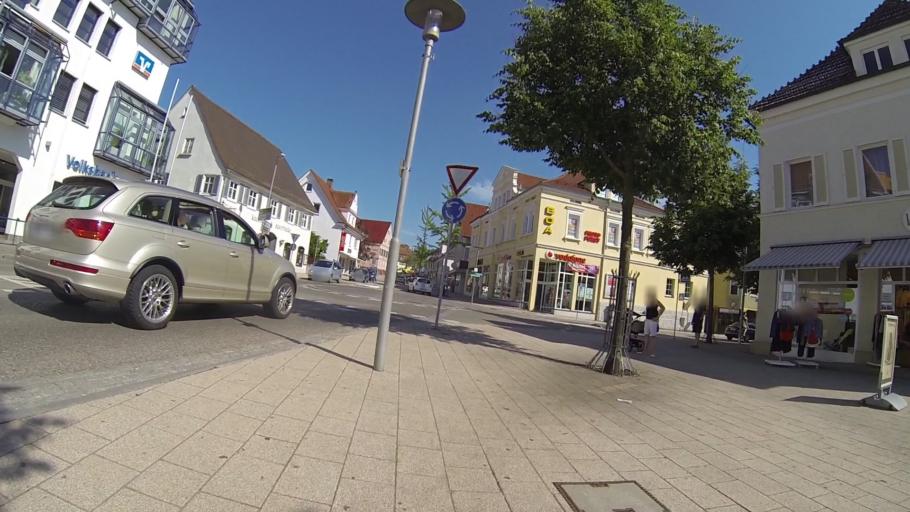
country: DE
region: Baden-Wuerttemberg
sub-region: Tuebingen Region
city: Laupheim
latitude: 48.2297
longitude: 9.8842
